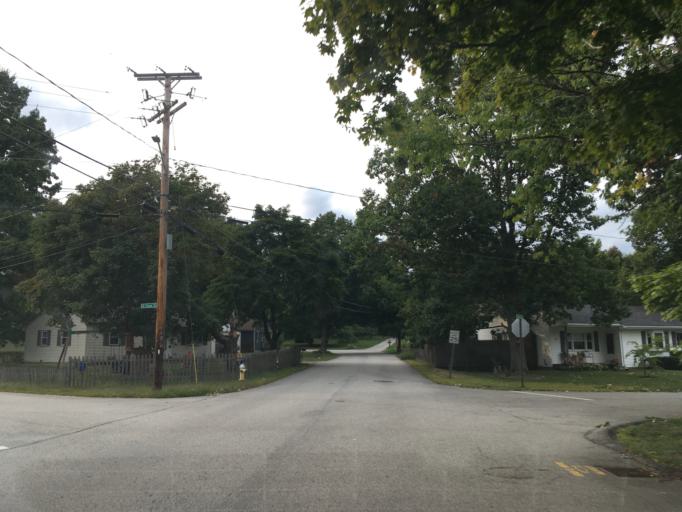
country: US
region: New Hampshire
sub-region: Rockingham County
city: Exeter
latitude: 42.9844
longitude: -70.9402
